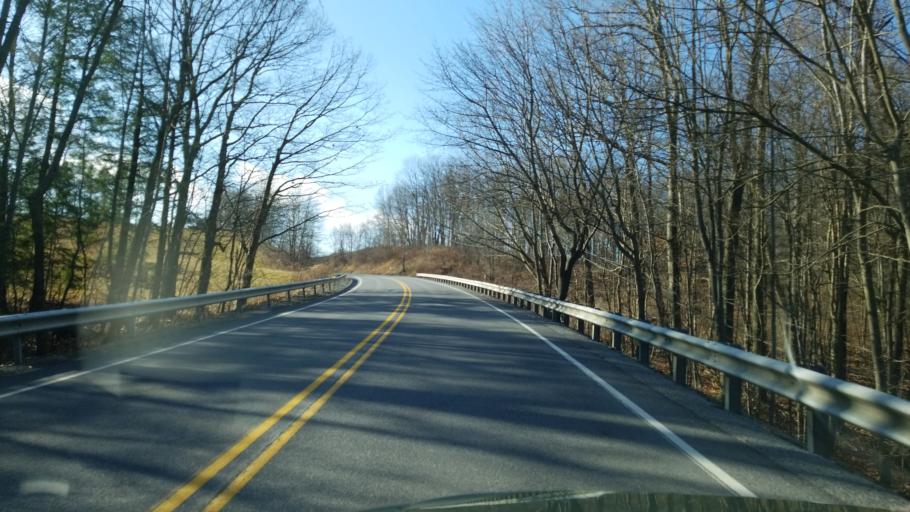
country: US
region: Pennsylvania
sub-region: Clearfield County
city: Hyde
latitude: 40.9994
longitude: -78.4404
